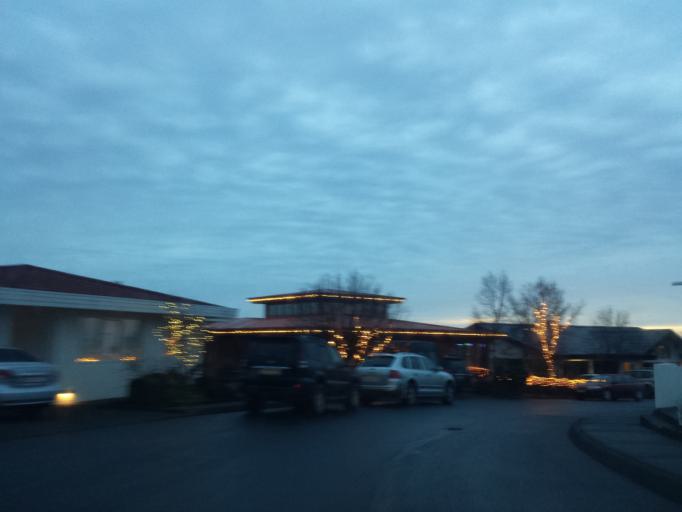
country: IS
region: Capital Region
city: Mosfellsbaer
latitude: 64.1349
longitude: -21.7739
